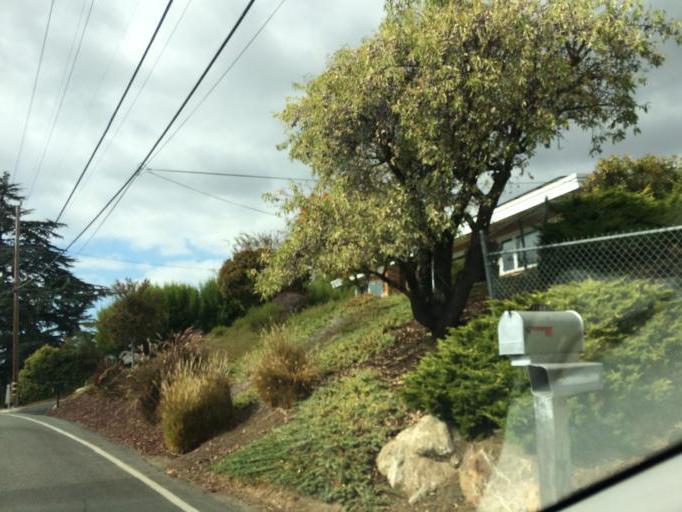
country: US
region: California
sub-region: Santa Clara County
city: East Foothills
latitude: 37.3916
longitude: -121.8194
